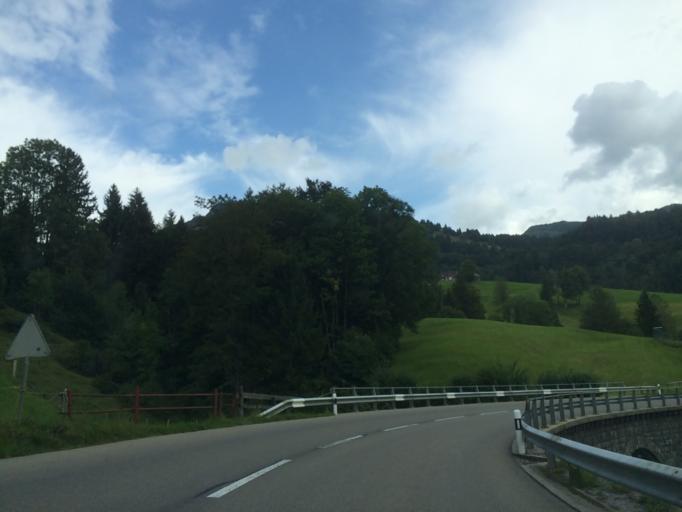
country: CH
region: Saint Gallen
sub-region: Wahlkreis Toggenburg
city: Krummenau
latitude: 47.2186
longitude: 9.2114
